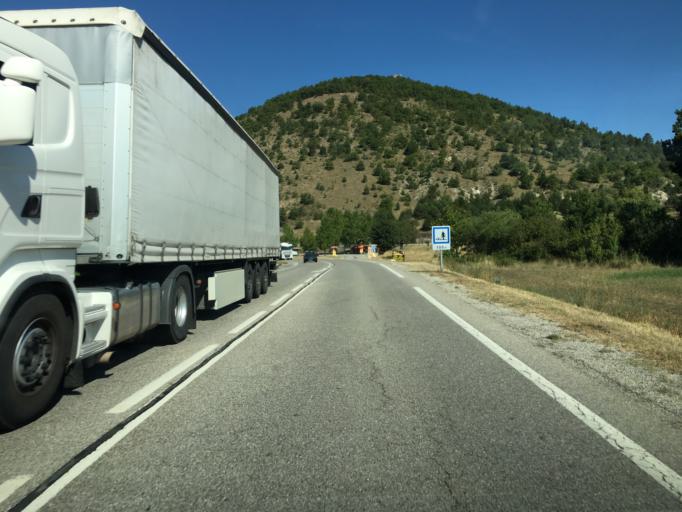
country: FR
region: Provence-Alpes-Cote d'Azur
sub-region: Departement des Hautes-Alpes
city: Serres
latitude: 44.3763
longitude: 5.7493
